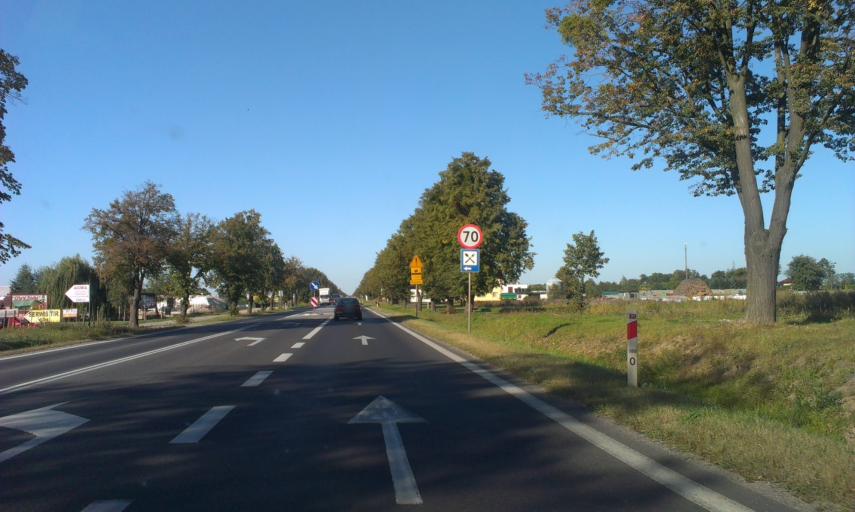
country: PL
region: Kujawsko-Pomorskie
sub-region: Powiat torunski
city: Lysomice
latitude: 53.0917
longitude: 18.6210
